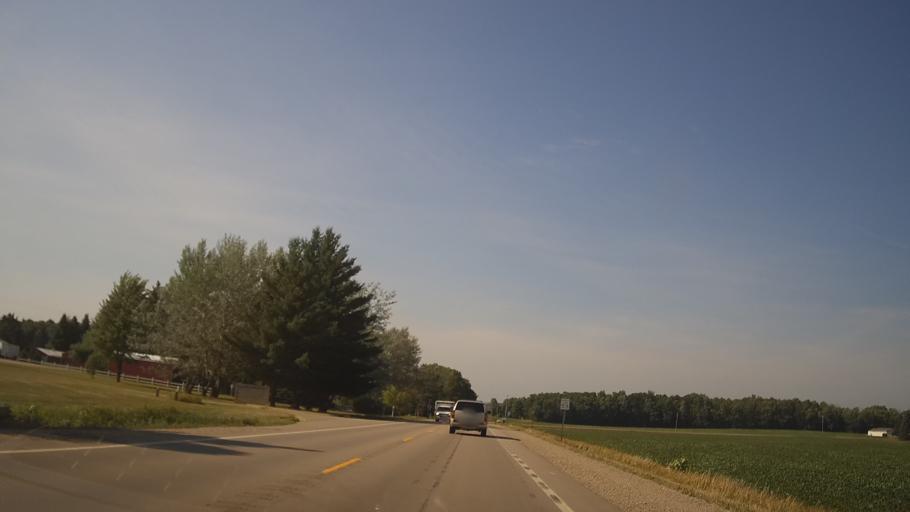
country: US
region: Michigan
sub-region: Ogemaw County
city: West Branch
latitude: 44.3096
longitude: -84.1258
